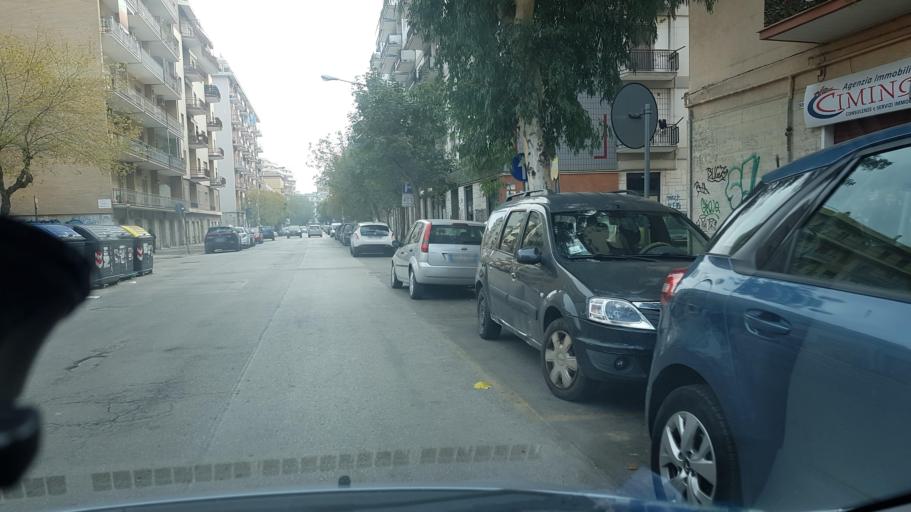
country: IT
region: Apulia
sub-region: Provincia di Foggia
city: Foggia
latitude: 41.4554
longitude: 15.5542
